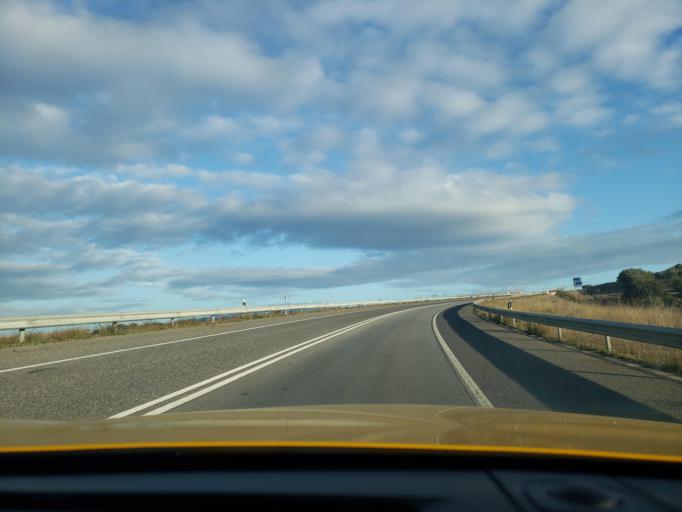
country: PT
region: Faro
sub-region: Portimao
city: Alvor
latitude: 37.1663
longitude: -8.5700
